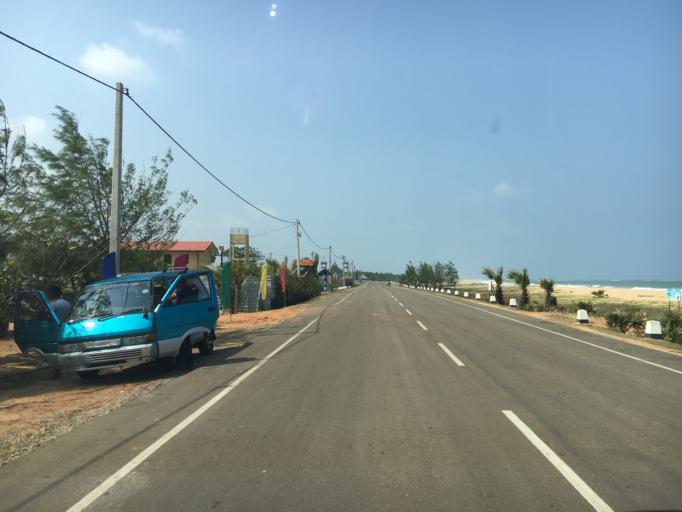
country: LK
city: Padaviya Divisional Secretariat
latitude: 9.2724
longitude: 80.8186
